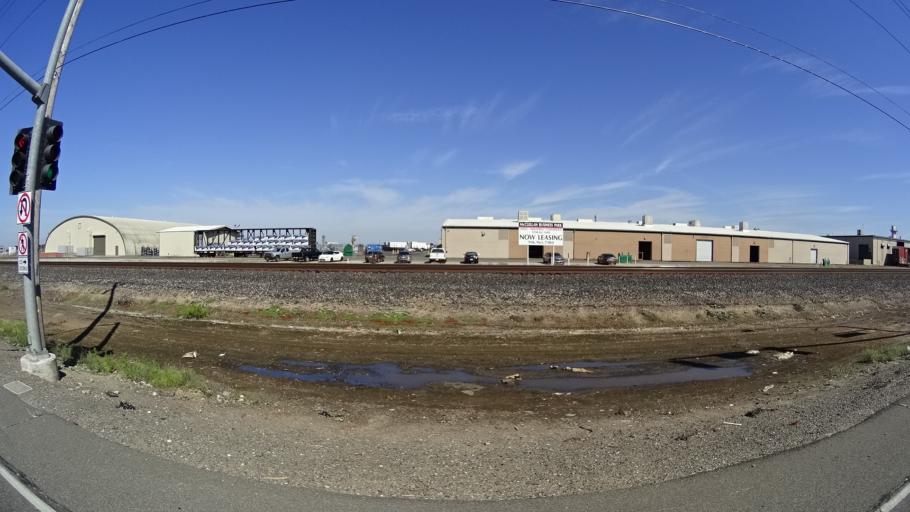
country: US
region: California
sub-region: Sacramento County
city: North Highlands
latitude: 38.6489
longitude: -121.3937
